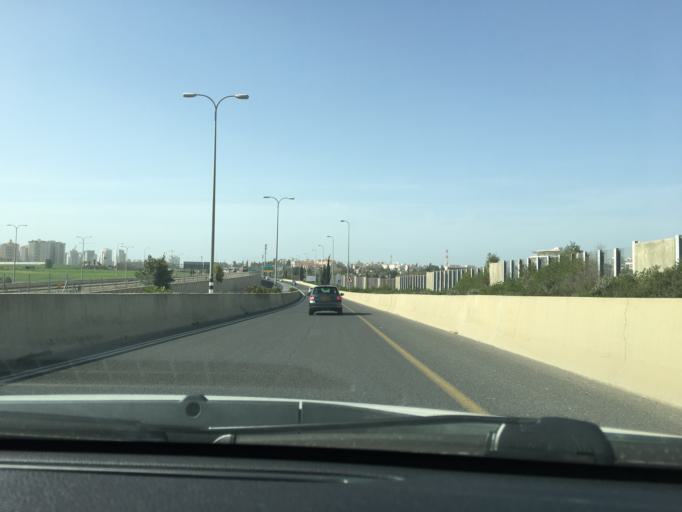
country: IL
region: Central District
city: Kfar Saba
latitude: 32.1654
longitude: 34.9251
